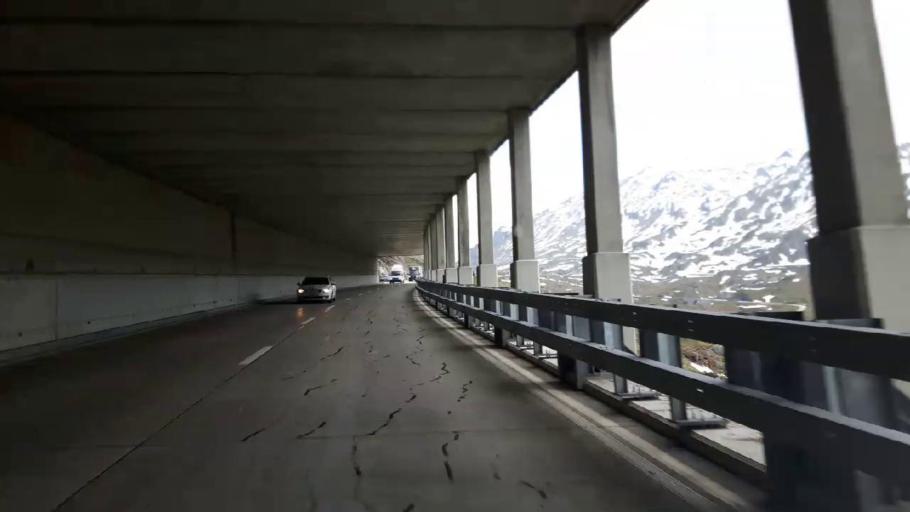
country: CH
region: Ticino
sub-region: Leventina District
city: Airolo
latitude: 46.5741
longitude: 8.5608
